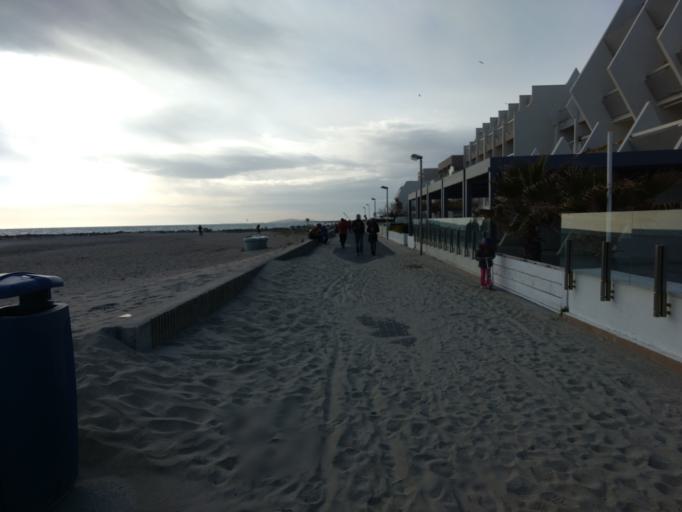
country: FR
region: Languedoc-Roussillon
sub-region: Departement de l'Herault
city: Palavas-les-Flots
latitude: 43.5201
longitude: 3.9146
